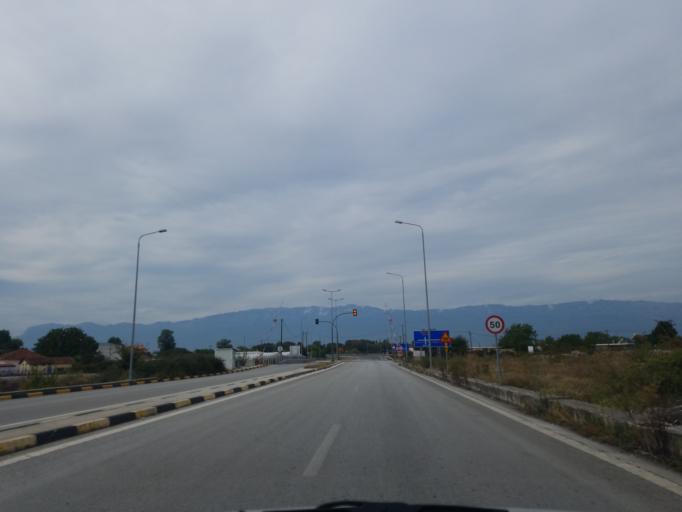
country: GR
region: Thessaly
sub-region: Trikala
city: Pyrgetos
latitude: 39.5721
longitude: 21.7467
